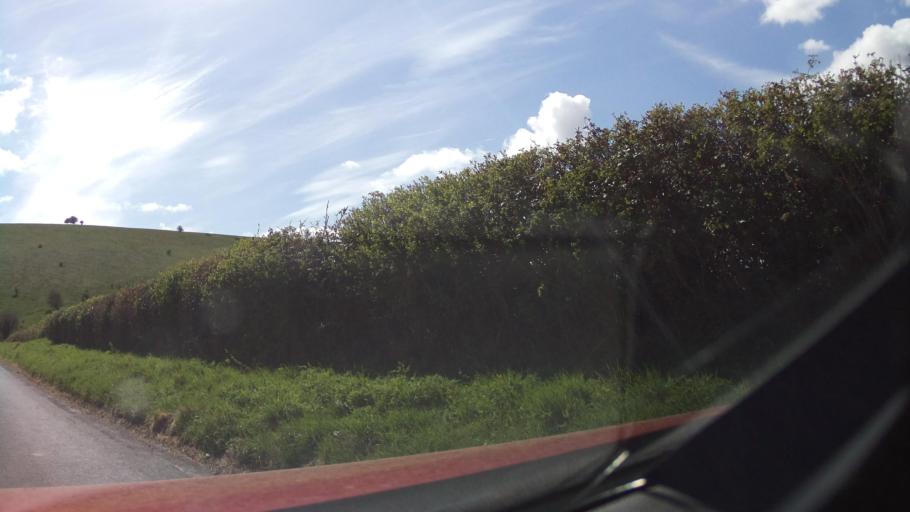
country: GB
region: England
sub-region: West Berkshire
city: Kintbury
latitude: 51.3622
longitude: -1.4755
